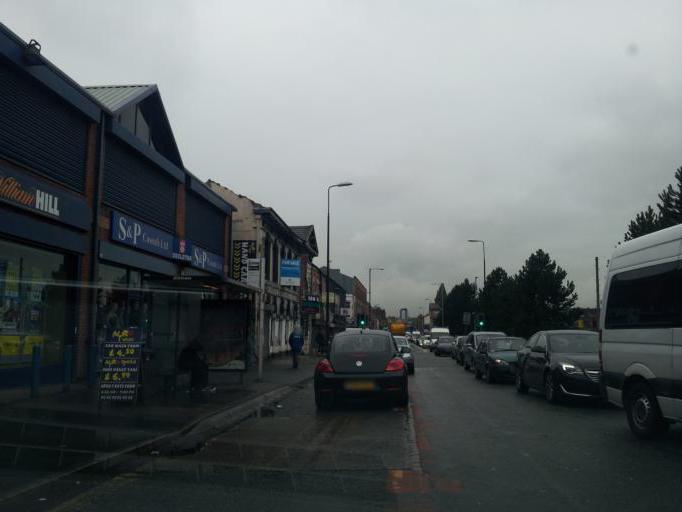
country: GB
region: England
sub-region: Manchester
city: Cheetham Hill
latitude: 53.4917
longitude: -2.2485
